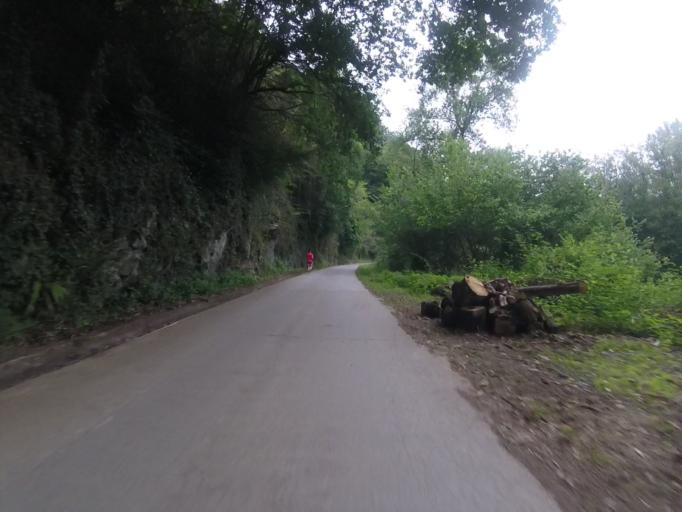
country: ES
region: Navarre
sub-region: Provincia de Navarra
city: Sunbilla
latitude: 43.1741
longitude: -1.6774
